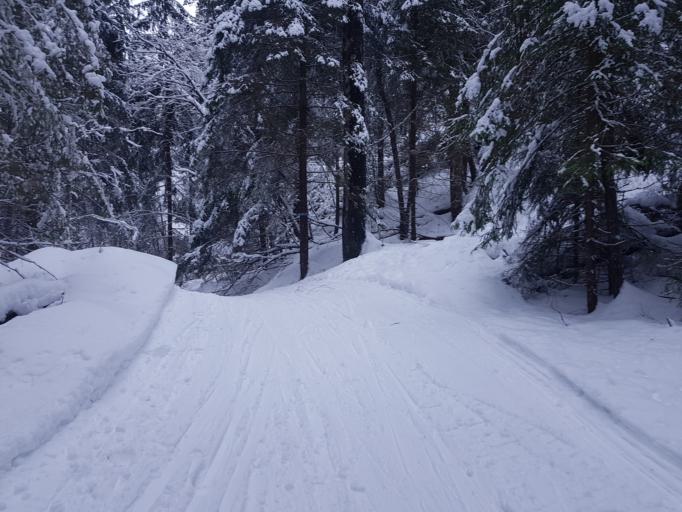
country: NO
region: Akershus
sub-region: Lorenskog
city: Kjenn
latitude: 59.8988
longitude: 10.8758
